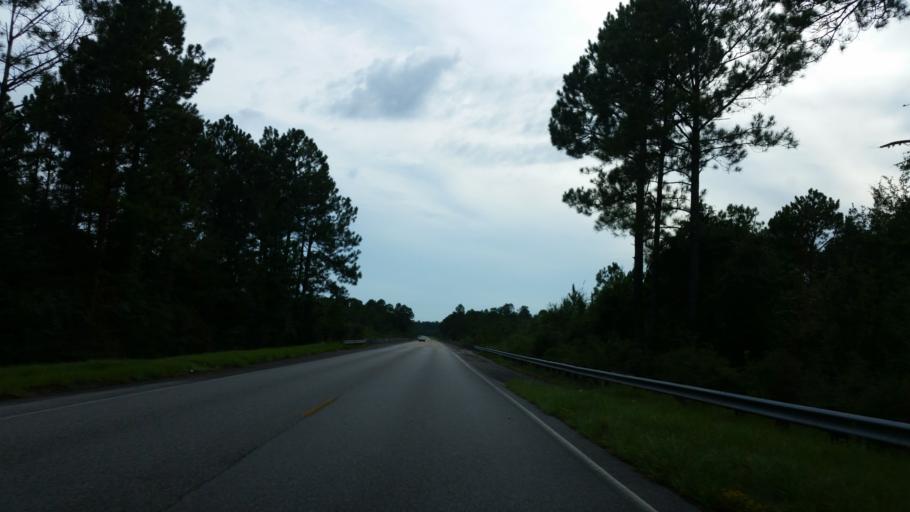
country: US
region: Florida
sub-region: Santa Rosa County
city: Point Baker
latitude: 30.7118
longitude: -86.9693
